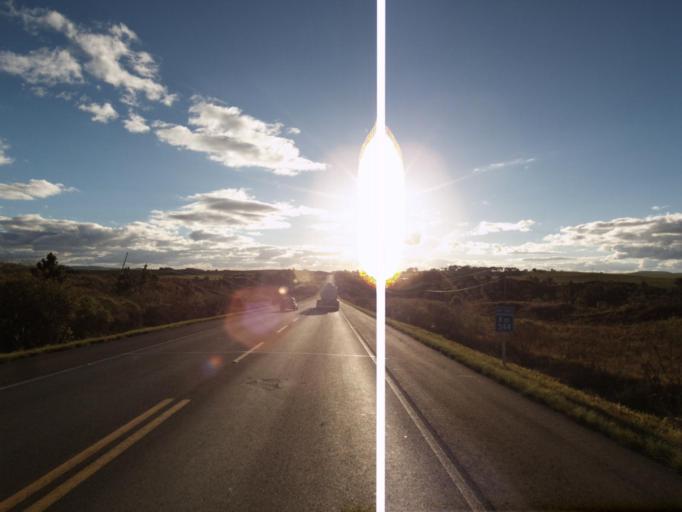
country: BR
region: Santa Catarina
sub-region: Campos Novos
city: Campos Novos
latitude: -27.3656
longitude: -51.2629
